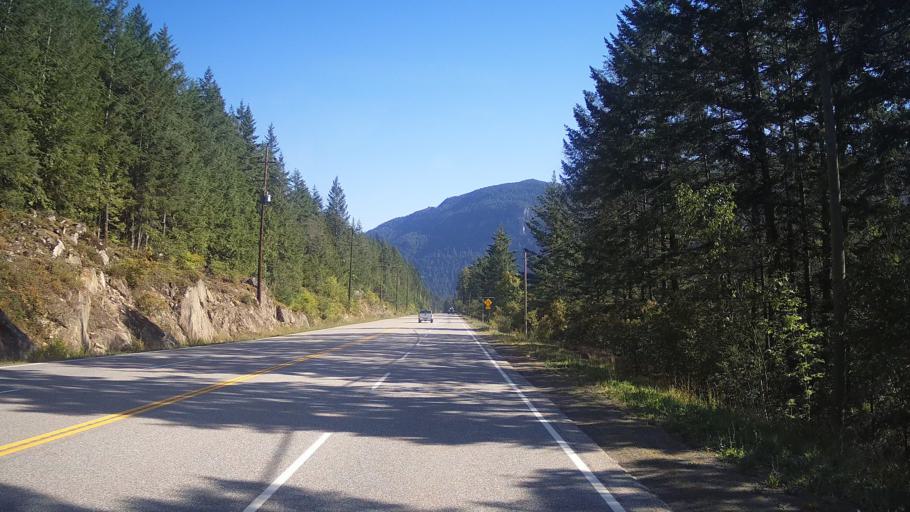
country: CA
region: British Columbia
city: Hope
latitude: 49.6769
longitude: -121.4184
